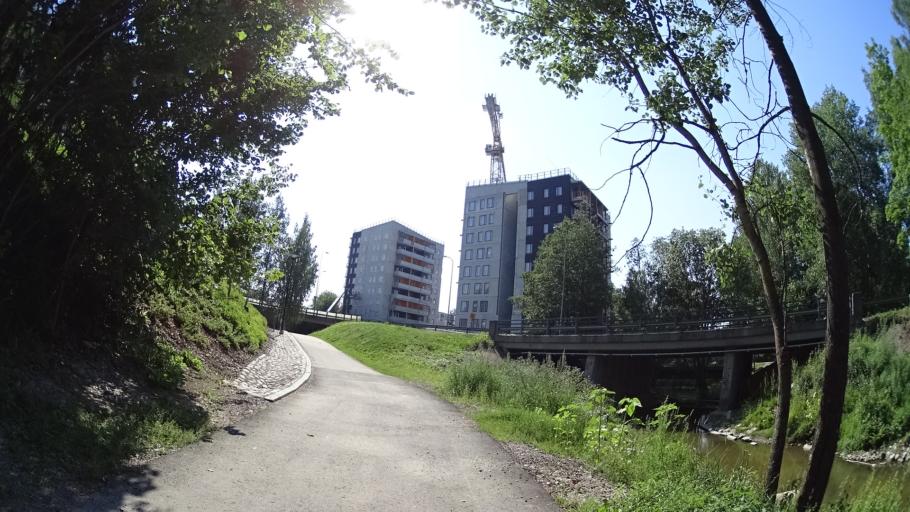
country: FI
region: Uusimaa
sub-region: Helsinki
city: Kerava
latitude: 60.3521
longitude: 25.0726
